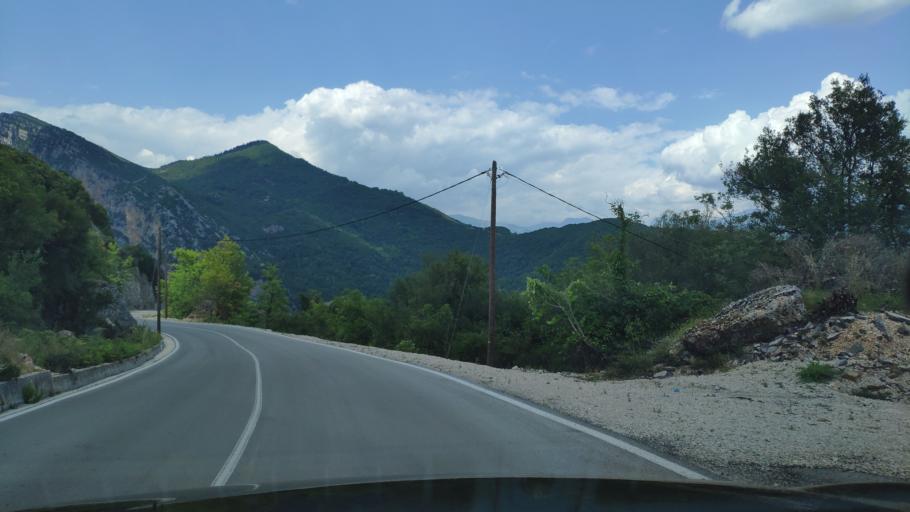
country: GR
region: Epirus
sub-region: Nomos Artas
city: Agios Dimitrios
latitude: 39.4603
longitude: 21.0230
